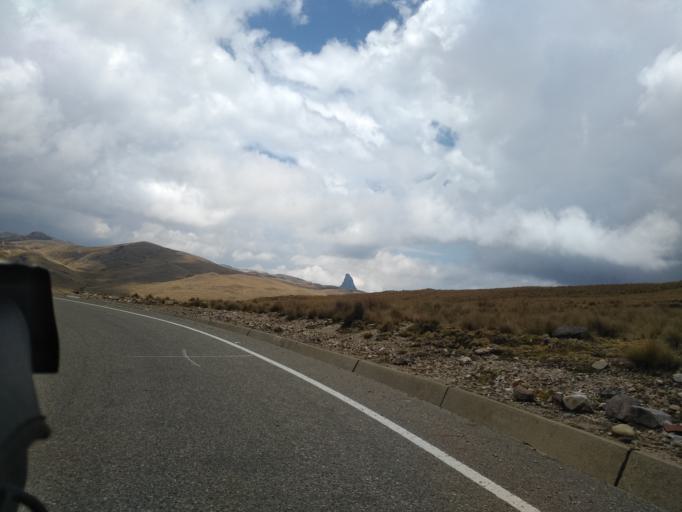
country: PE
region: La Libertad
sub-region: Provincia de Santiago de Chuco
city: Quiruvilca
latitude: -7.9706
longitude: -78.2062
